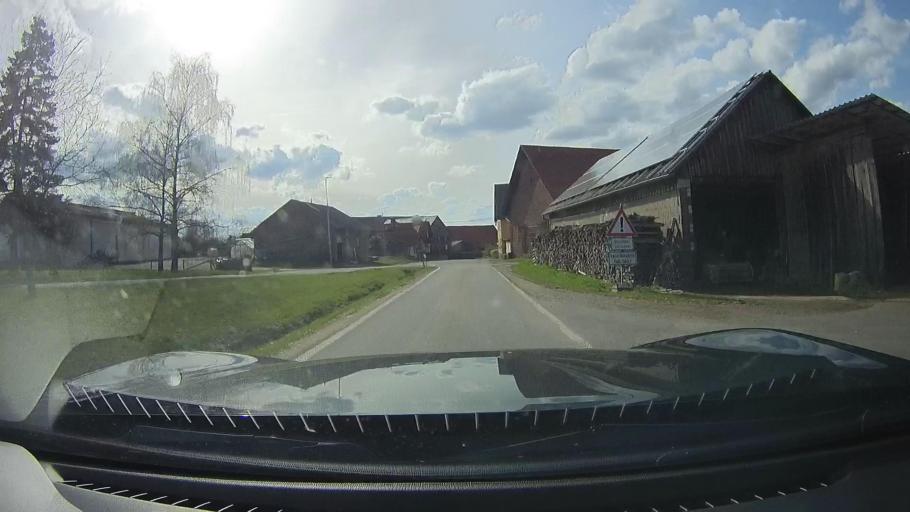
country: DE
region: Bavaria
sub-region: Regierungsbezirk Unterfranken
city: Weilbach
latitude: 49.6220
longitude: 9.2677
